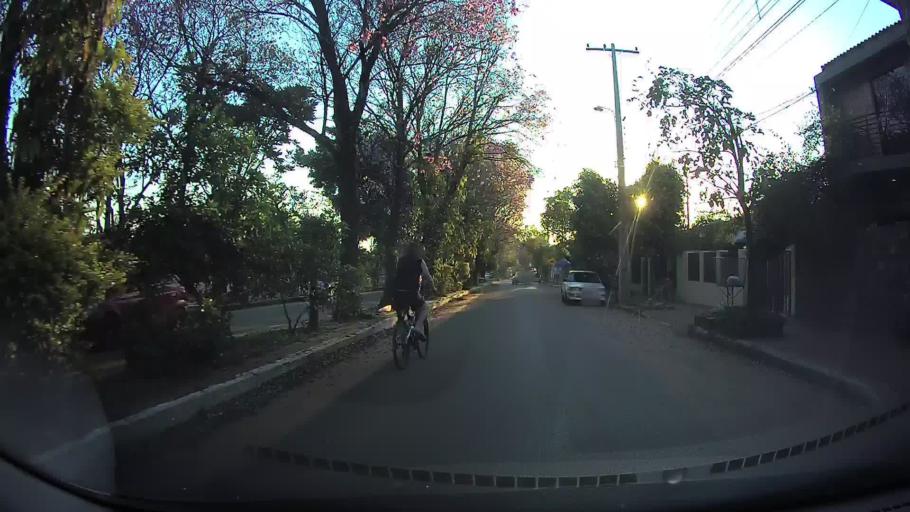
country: PY
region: Central
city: Limpio
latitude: -25.2362
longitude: -57.4784
